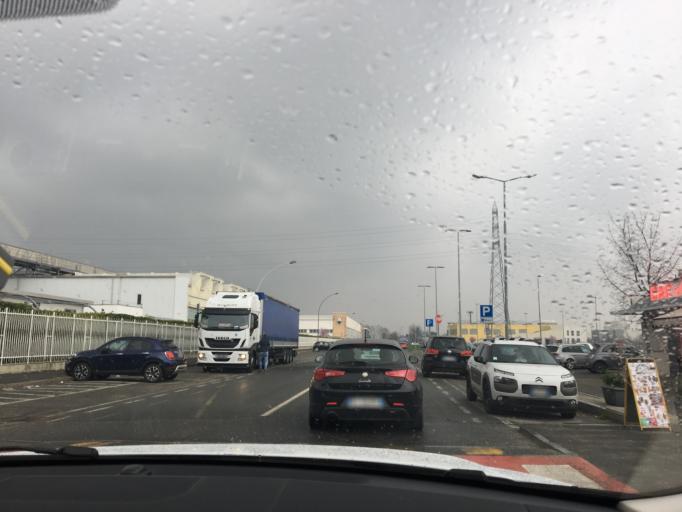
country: IT
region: Piedmont
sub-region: Provincia di Torino
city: Grugliasco
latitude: 45.0484
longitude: 7.5922
